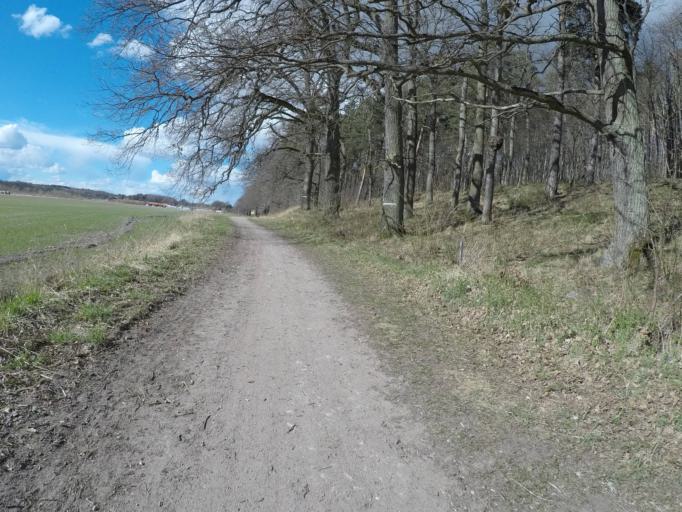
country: SE
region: Vaestmanland
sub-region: Hallstahammars Kommun
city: Kolback
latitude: 59.5138
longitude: 16.2578
